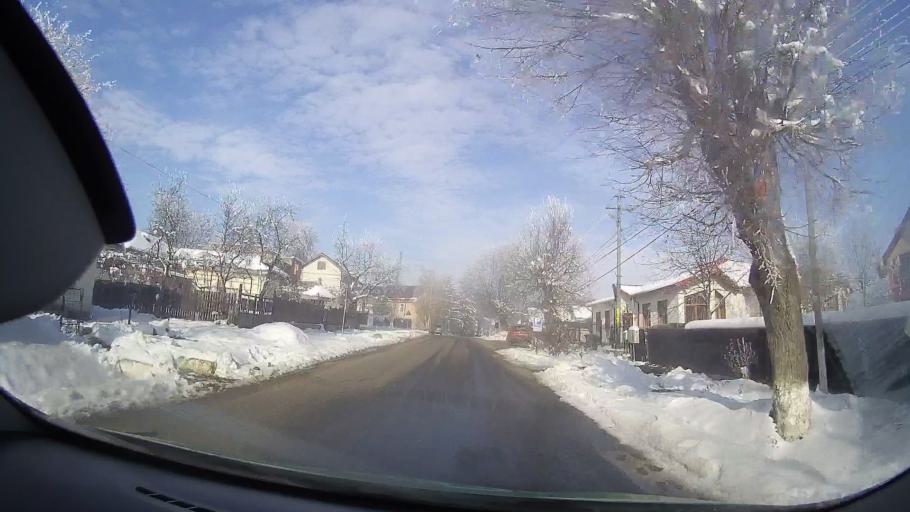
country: RO
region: Iasi
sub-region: Comuna Cristesti
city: Cristesti
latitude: 47.2590
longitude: 26.5749
